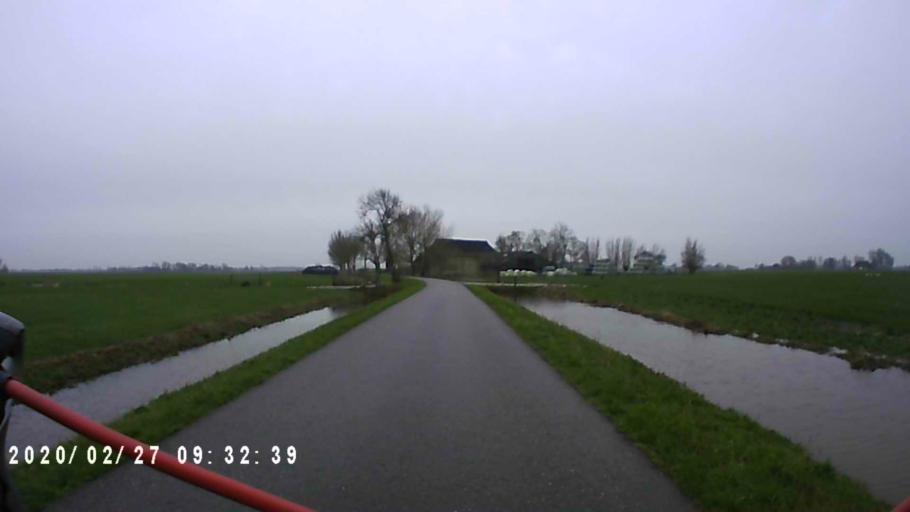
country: NL
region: Groningen
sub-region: Gemeente Zuidhorn
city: Aduard
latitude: 53.2902
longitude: 6.4491
